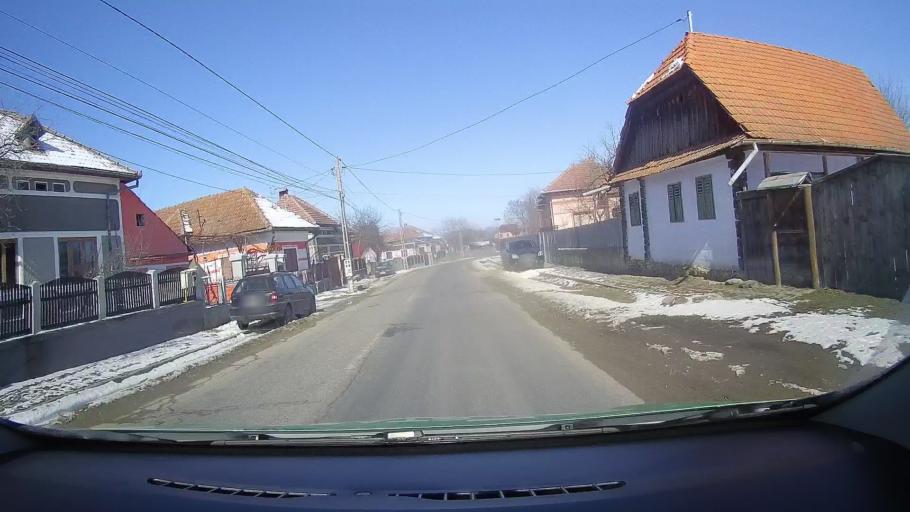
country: RO
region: Brasov
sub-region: Oras Victoria
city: Victoria
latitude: 45.7496
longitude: 24.7391
